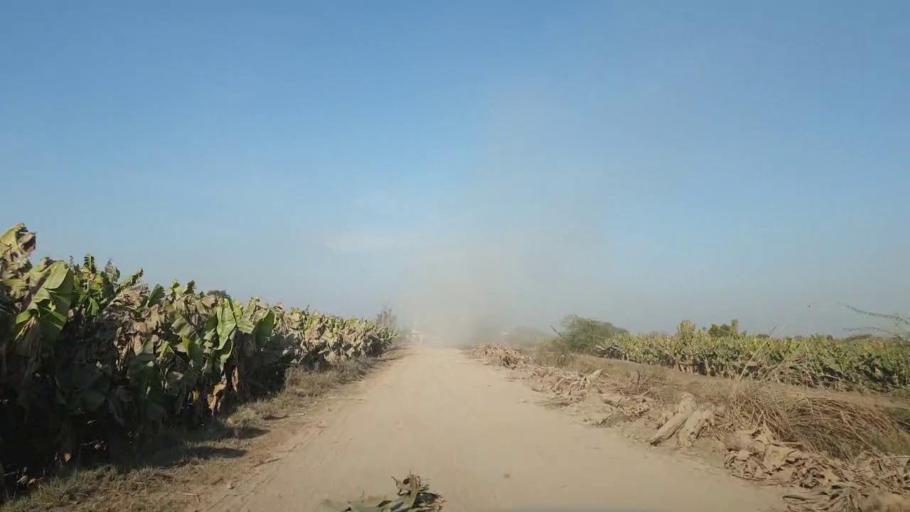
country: PK
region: Sindh
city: Tando Adam
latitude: 25.7074
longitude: 68.7026
